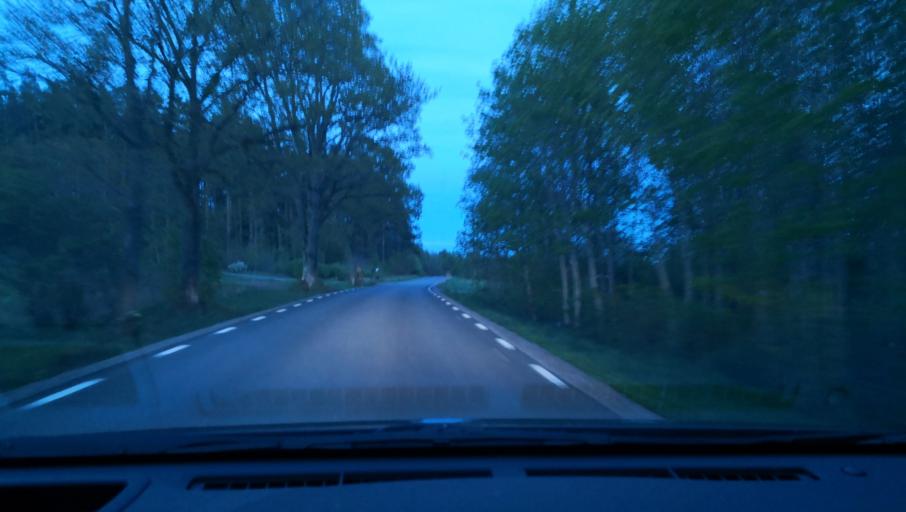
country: SE
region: OErebro
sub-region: Askersunds Kommun
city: Asbro
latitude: 59.0686
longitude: 14.9835
